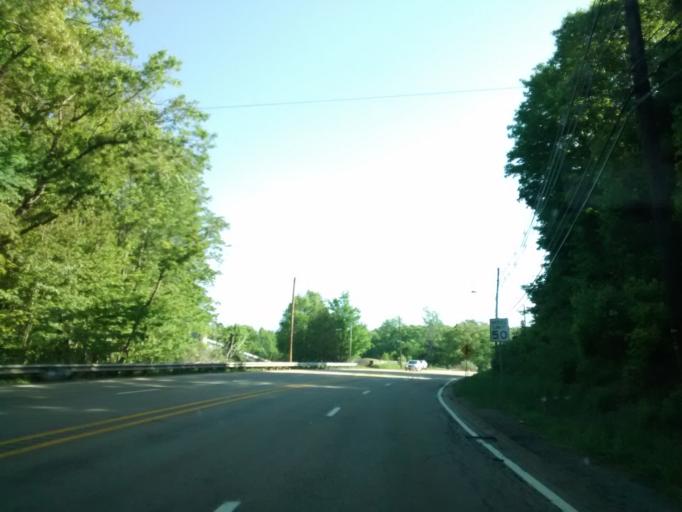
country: US
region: Massachusetts
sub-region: Worcester County
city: Sturbridge
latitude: 42.1312
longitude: -72.0426
